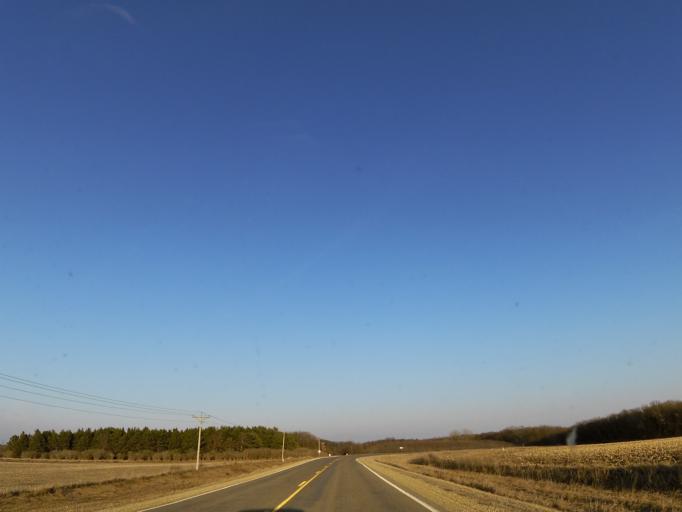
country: US
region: Iowa
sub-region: Mitchell County
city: Saint Ansgar
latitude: 43.3930
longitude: -92.9478
